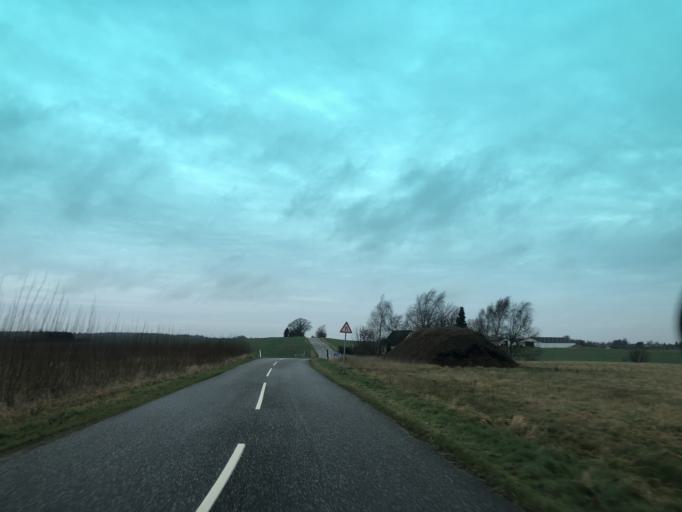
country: DK
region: Capital Region
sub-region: Allerod Kommune
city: Lynge
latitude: 55.8532
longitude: 12.2406
